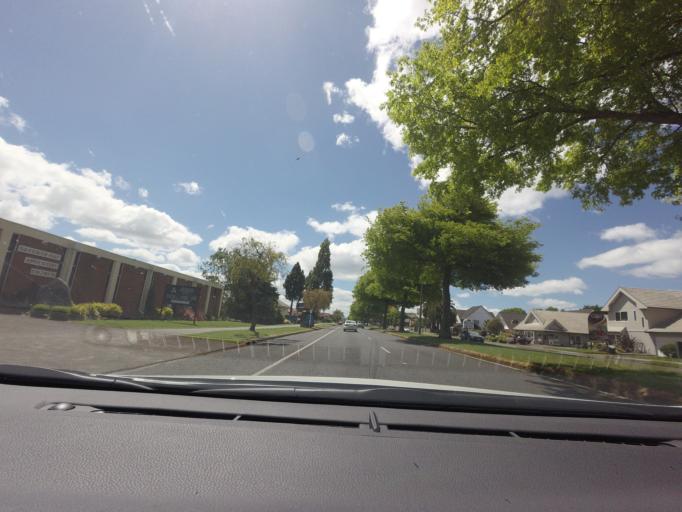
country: NZ
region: Bay of Plenty
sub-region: Rotorua District
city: Rotorua
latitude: -38.1509
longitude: 176.2537
